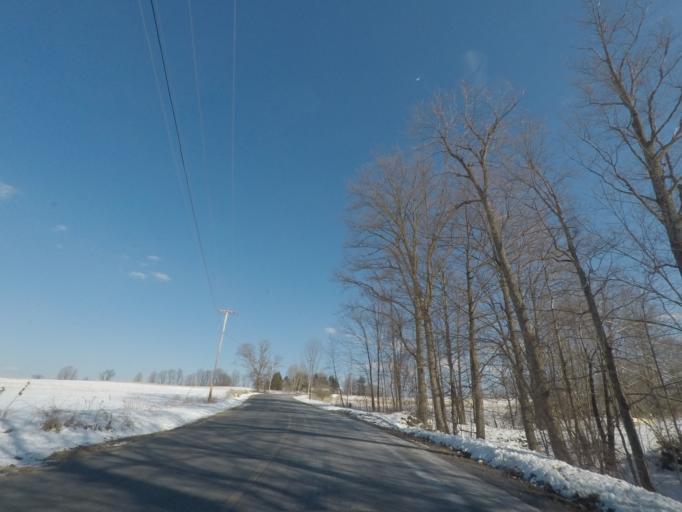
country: US
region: New York
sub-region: Rensselaer County
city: Hoosick Falls
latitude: 42.8711
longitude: -73.4963
